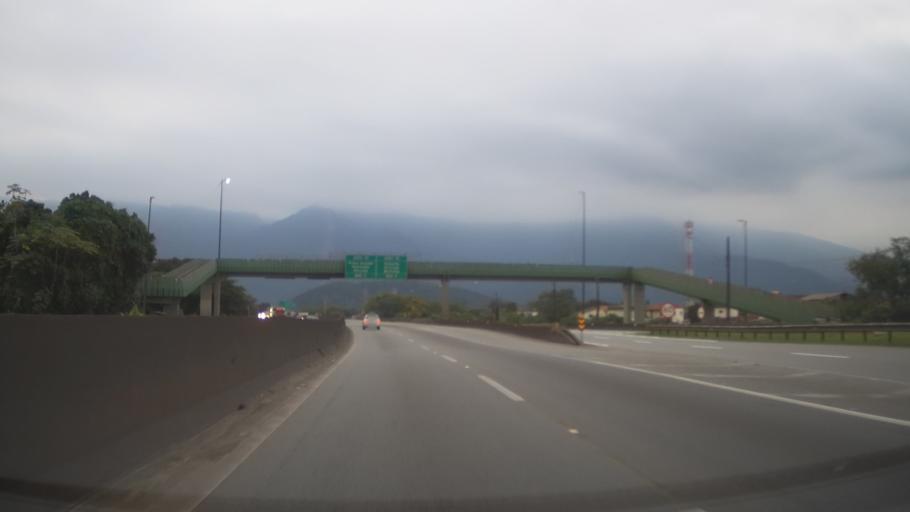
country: BR
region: Sao Paulo
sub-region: Cubatao
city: Cubatao
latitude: -23.9005
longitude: -46.4289
